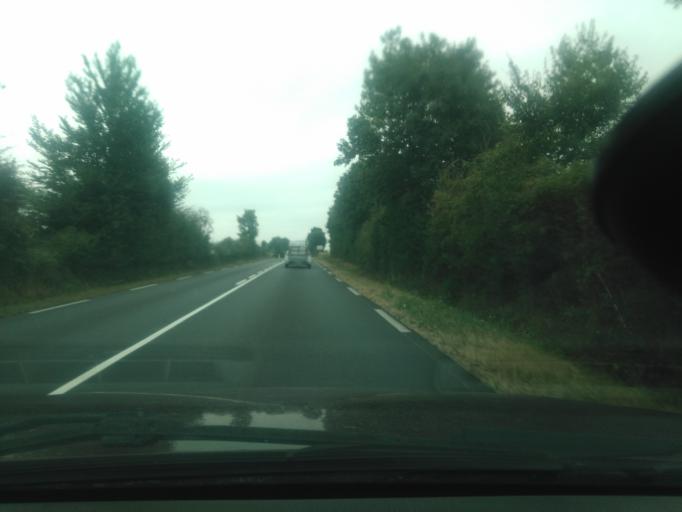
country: FR
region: Pays de la Loire
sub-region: Departement de la Vendee
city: Bazoges-en-Pareds
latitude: 46.6779
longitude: -0.9118
